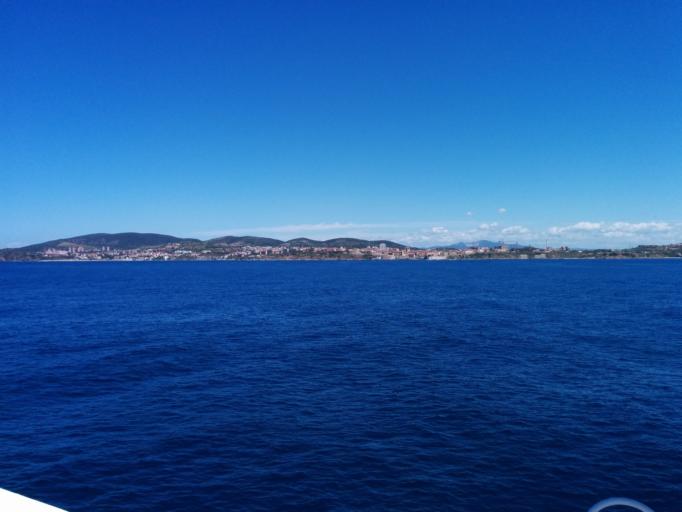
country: IT
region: Tuscany
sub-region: Provincia di Livorno
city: Piombino
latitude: 42.9017
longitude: 10.5175
